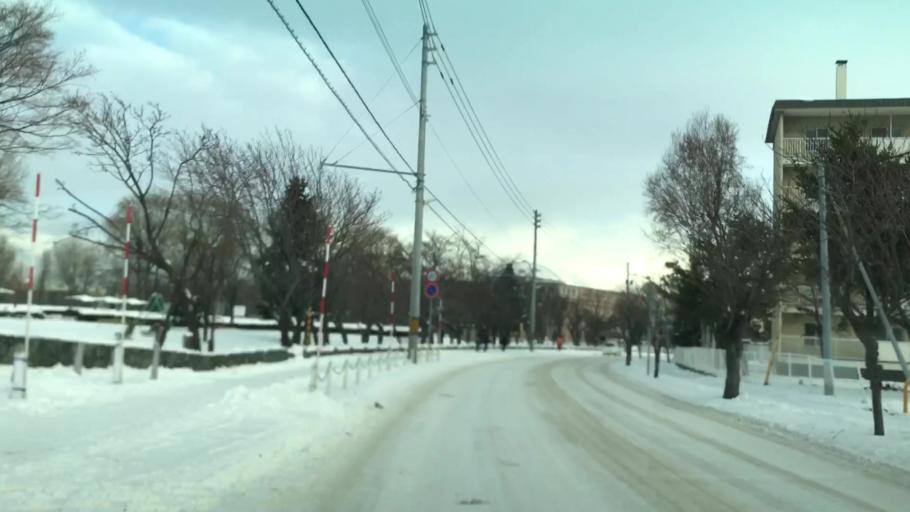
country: JP
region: Hokkaido
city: Sapporo
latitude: 43.0887
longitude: 141.3042
